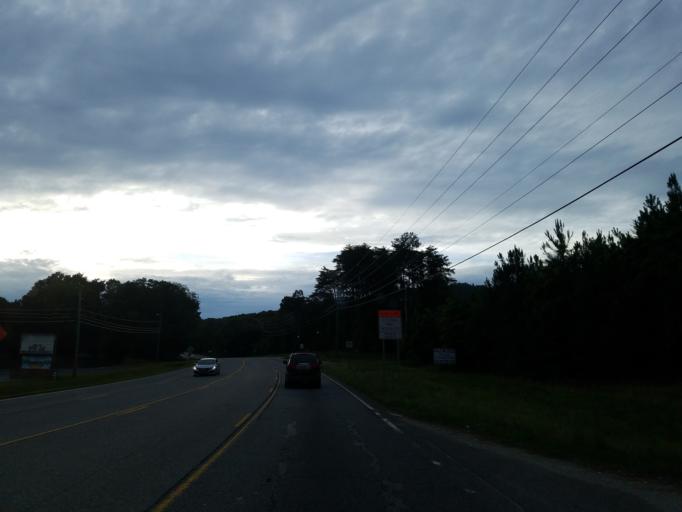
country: US
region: Georgia
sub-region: Forsyth County
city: Cumming
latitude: 34.2218
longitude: -84.1543
